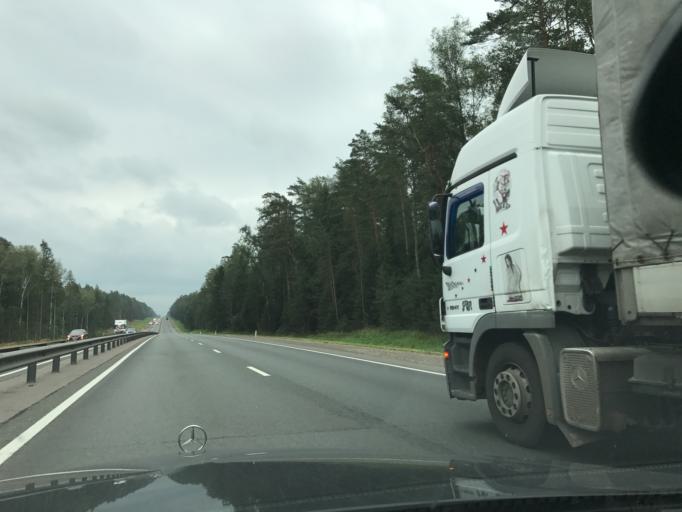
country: RU
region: Vladimir
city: Kameshkovo
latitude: 56.1974
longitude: 41.0133
